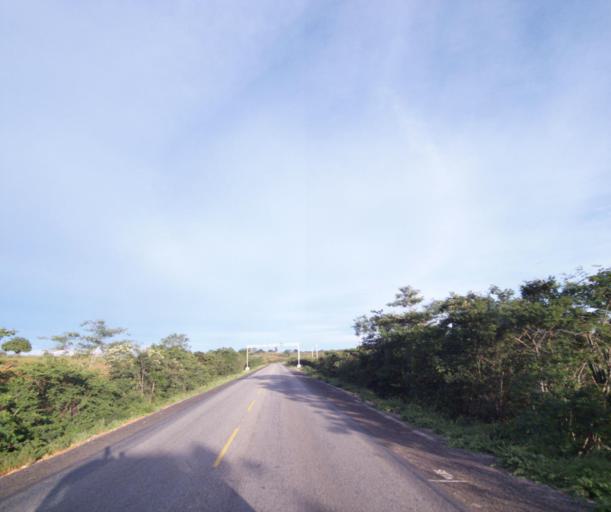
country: BR
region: Bahia
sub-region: Cacule
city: Cacule
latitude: -14.2093
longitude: -42.1024
